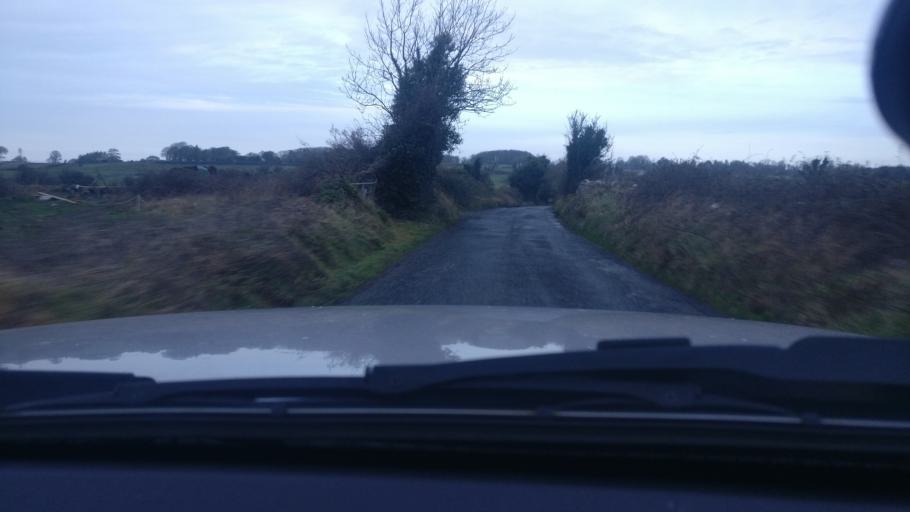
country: IE
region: Connaught
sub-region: County Galway
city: Loughrea
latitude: 53.1712
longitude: -8.5084
